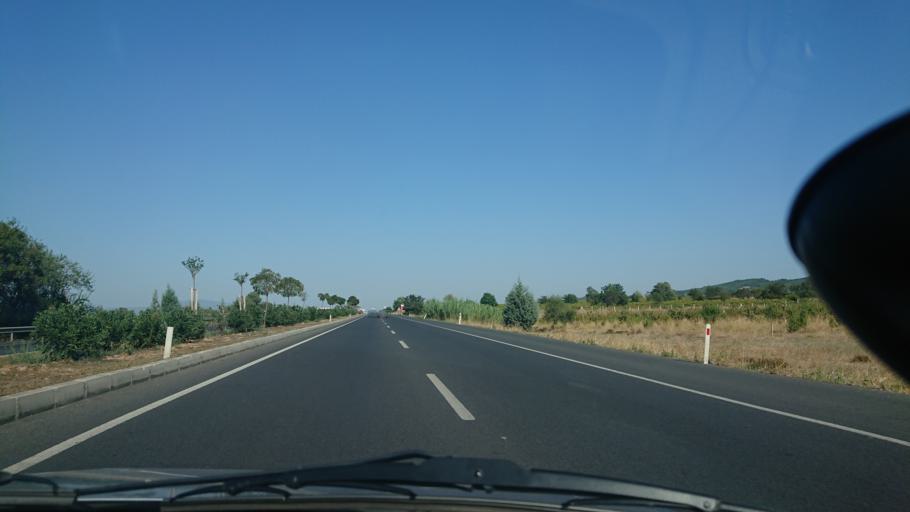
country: TR
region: Manisa
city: Ahmetli
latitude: 38.5064
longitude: 27.8895
